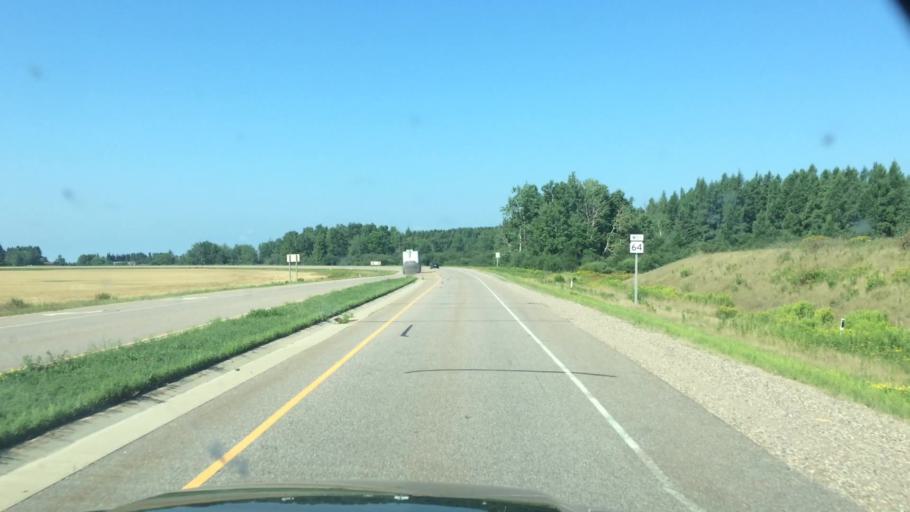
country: US
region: Wisconsin
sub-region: Langlade County
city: Antigo
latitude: 45.1528
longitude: -89.1791
